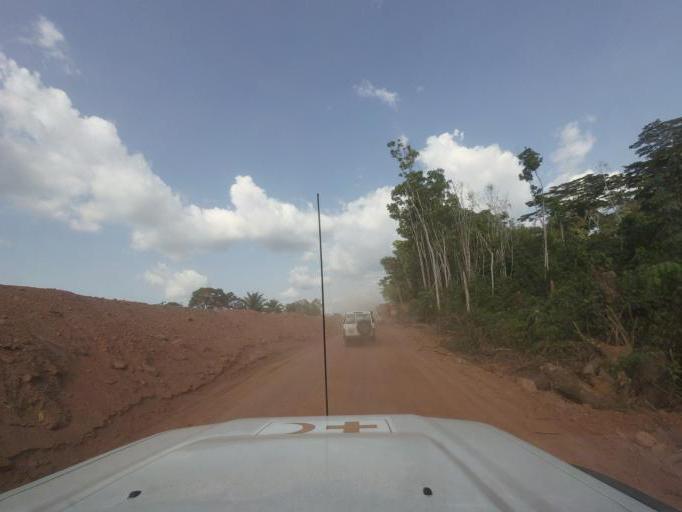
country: LR
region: Bong
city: Gbarnga
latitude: 7.0410
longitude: -9.5403
